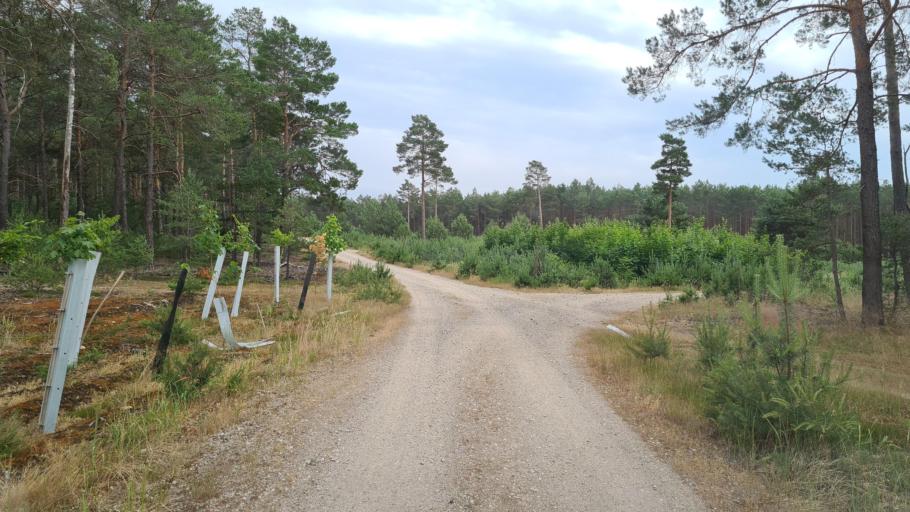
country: DE
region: Brandenburg
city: Schilda
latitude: 51.6577
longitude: 13.3406
